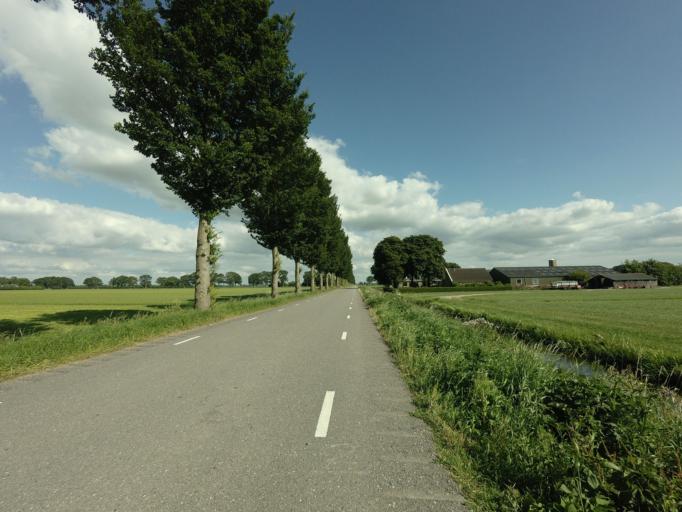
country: NL
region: North Holland
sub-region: Gemeente Uithoorn
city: Uithoorn
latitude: 52.2036
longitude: 4.8253
